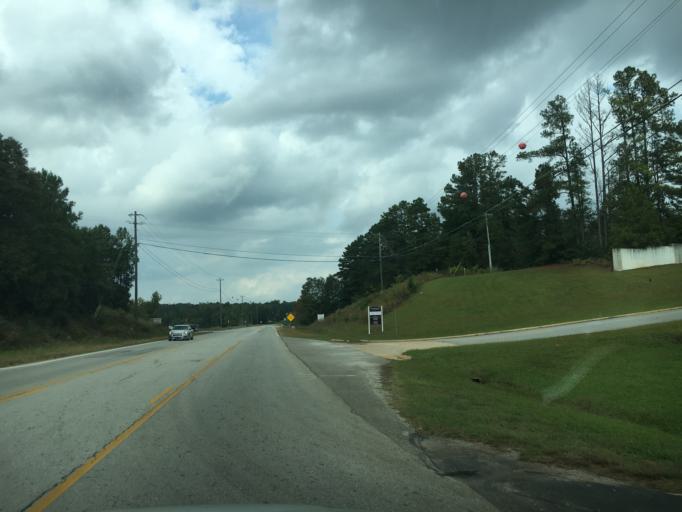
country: US
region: Georgia
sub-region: Hart County
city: Hartwell
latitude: 34.3824
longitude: -82.9405
